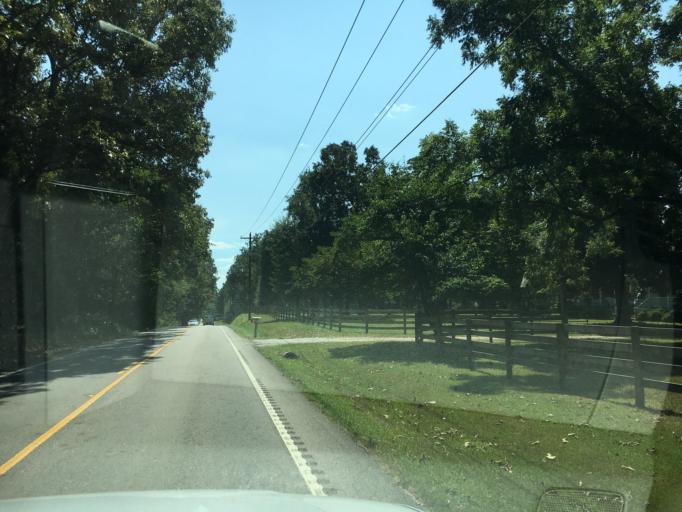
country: US
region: South Carolina
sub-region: Aiken County
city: Aiken
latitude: 33.5126
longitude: -81.6867
